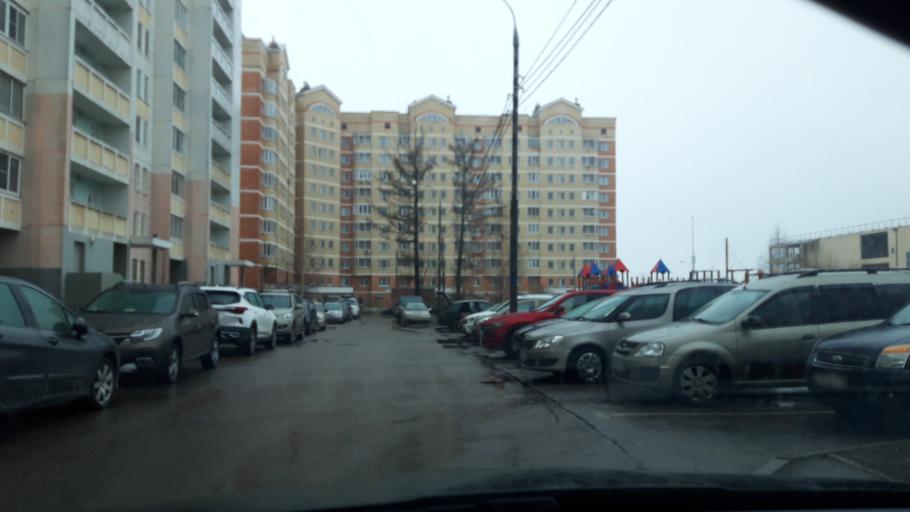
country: RU
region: Moscow
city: Zelenograd
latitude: 55.9719
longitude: 37.1661
